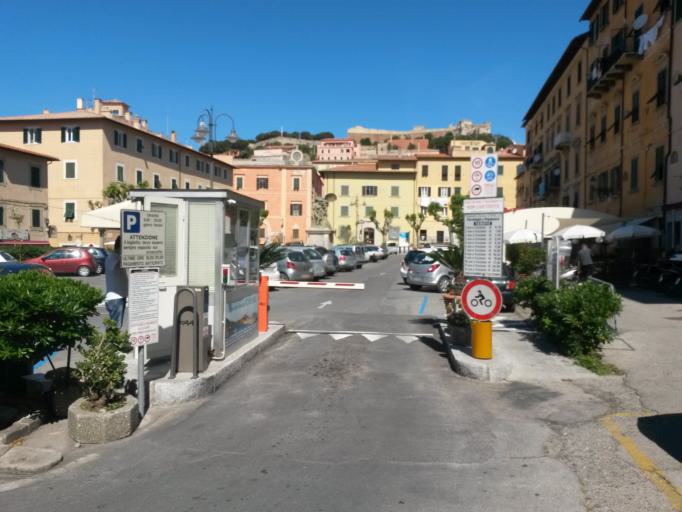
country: IT
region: Tuscany
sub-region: Provincia di Livorno
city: Portoferraio
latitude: 42.8149
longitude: 10.3324
